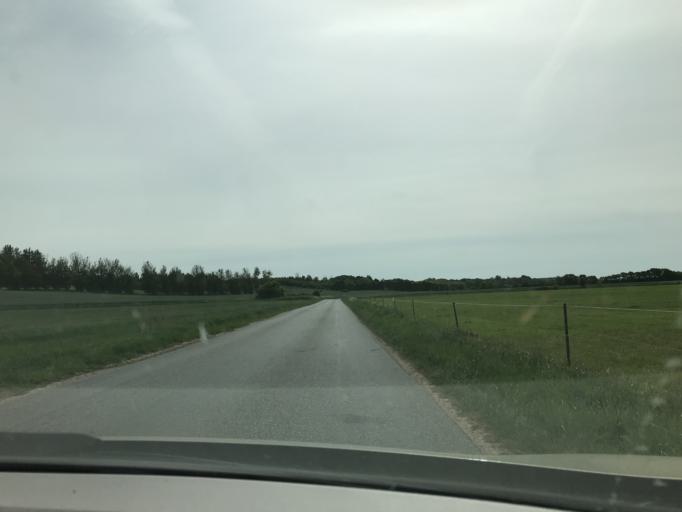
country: DK
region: Central Jutland
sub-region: Norddjurs Kommune
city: Allingabro
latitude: 56.5861
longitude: 10.3098
